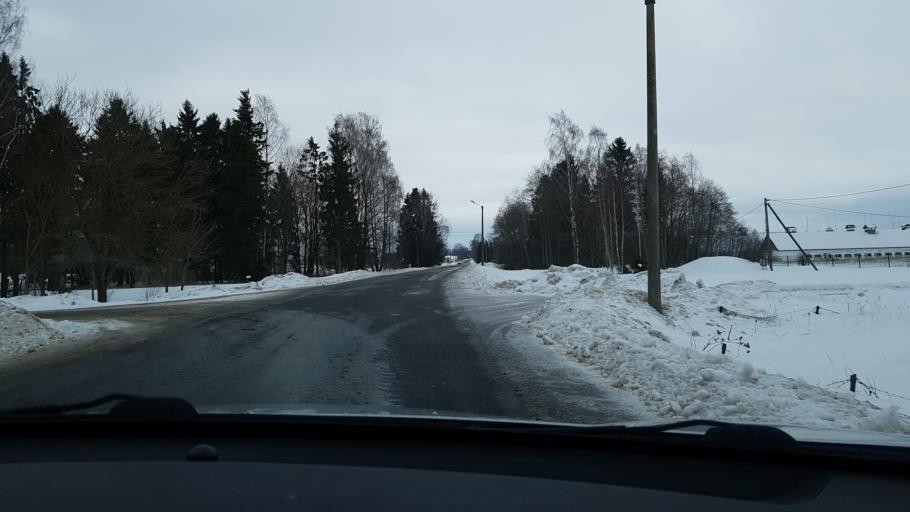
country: EE
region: Jaervamaa
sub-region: Koeru vald
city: Koeru
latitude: 58.9714
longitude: 26.0117
